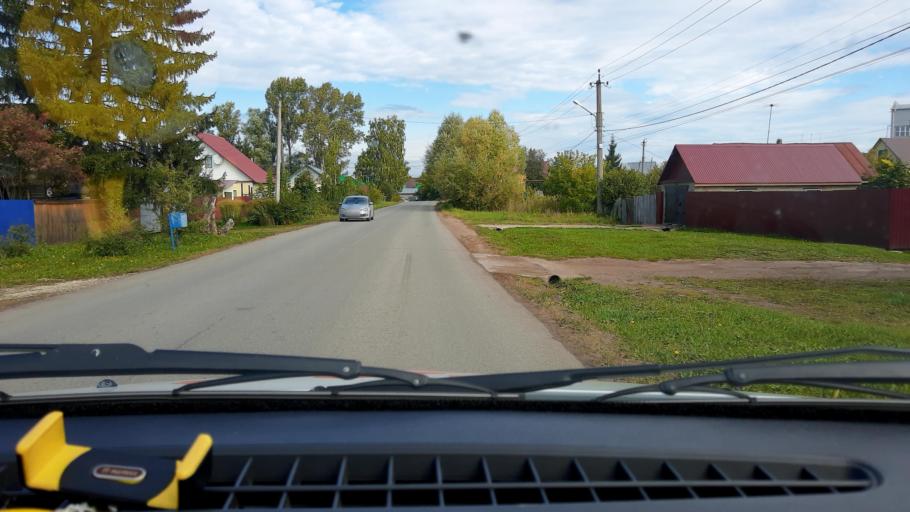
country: RU
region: Bashkortostan
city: Blagoveshchensk
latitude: 55.0356
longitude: 55.9831
